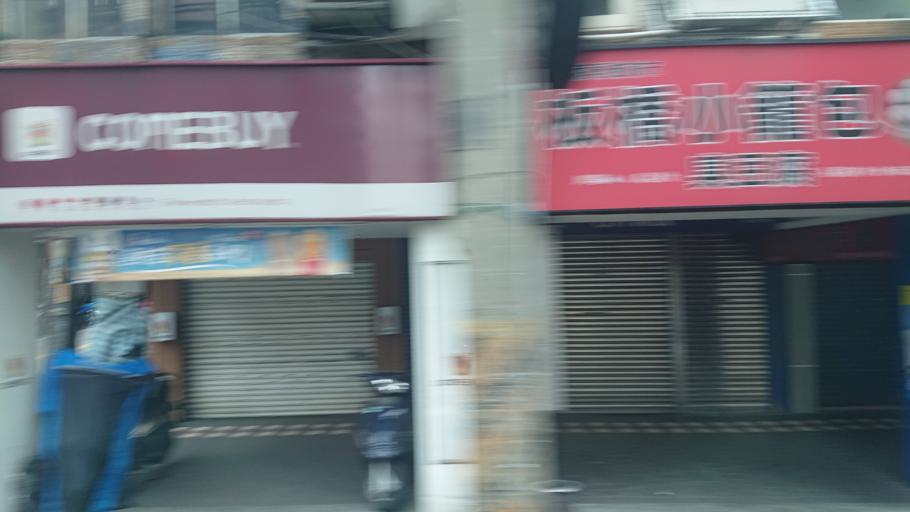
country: TW
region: Taipei
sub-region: Taipei
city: Banqiao
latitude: 25.0055
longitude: 121.4557
